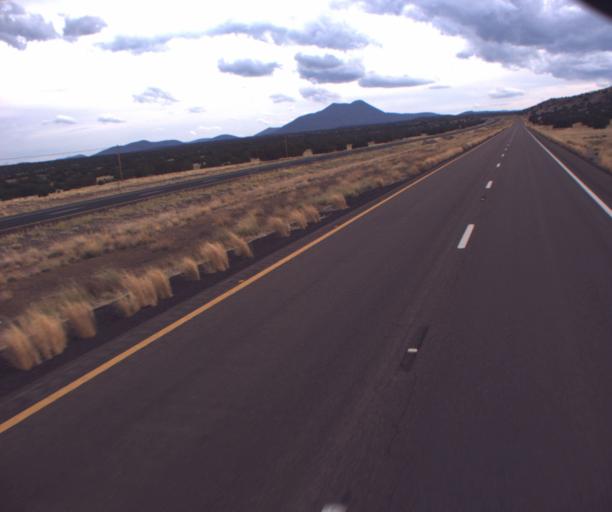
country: US
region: Arizona
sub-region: Coconino County
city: Flagstaff
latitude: 35.5325
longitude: -111.5411
